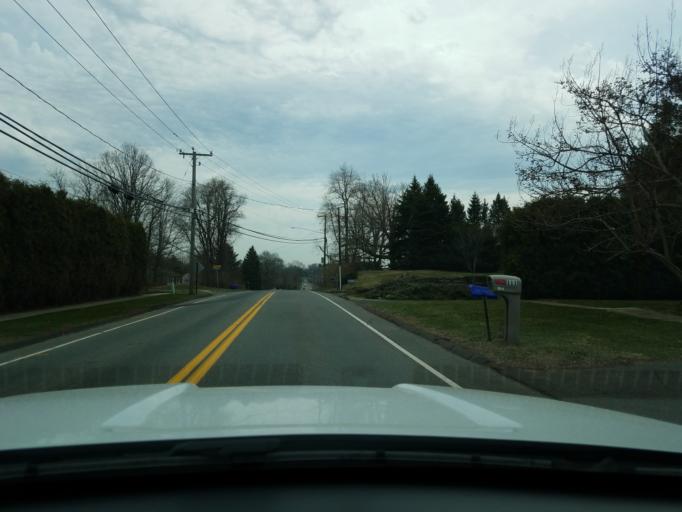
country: US
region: Connecticut
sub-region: Hartford County
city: Newington
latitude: 41.6683
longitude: -72.6878
